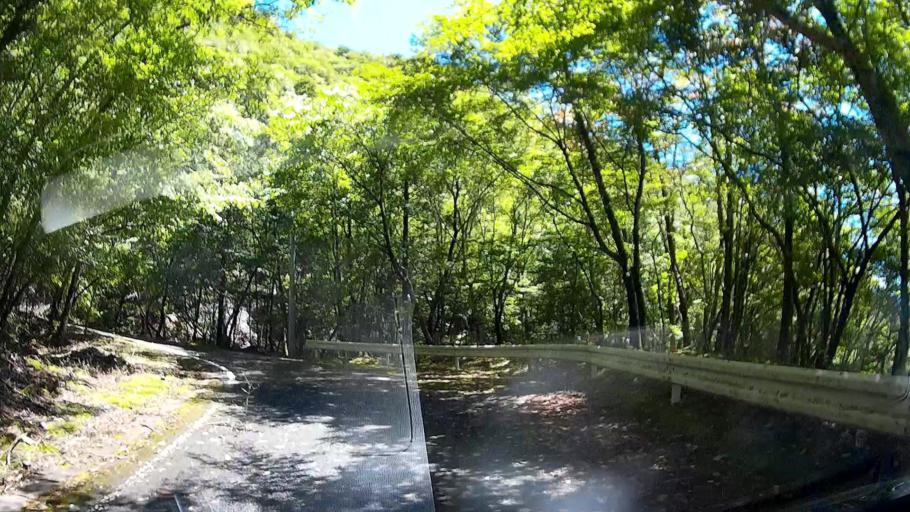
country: JP
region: Shizuoka
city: Fujinomiya
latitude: 35.3001
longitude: 138.3137
